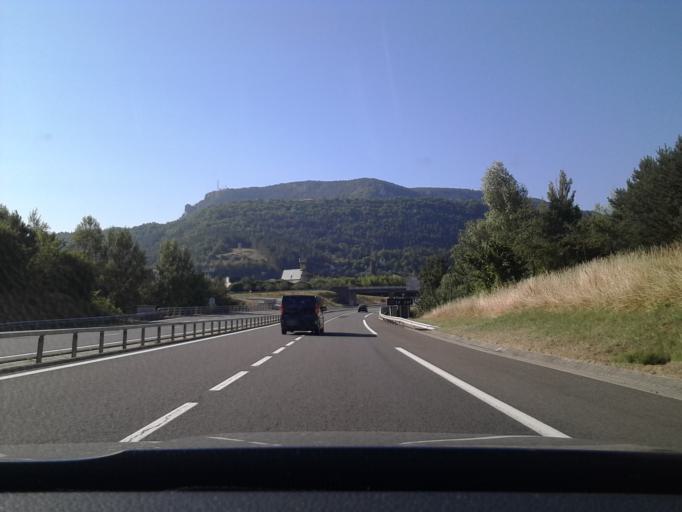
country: FR
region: Languedoc-Roussillon
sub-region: Departement de la Lozere
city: La Canourgue
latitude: 44.4399
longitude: 3.1947
